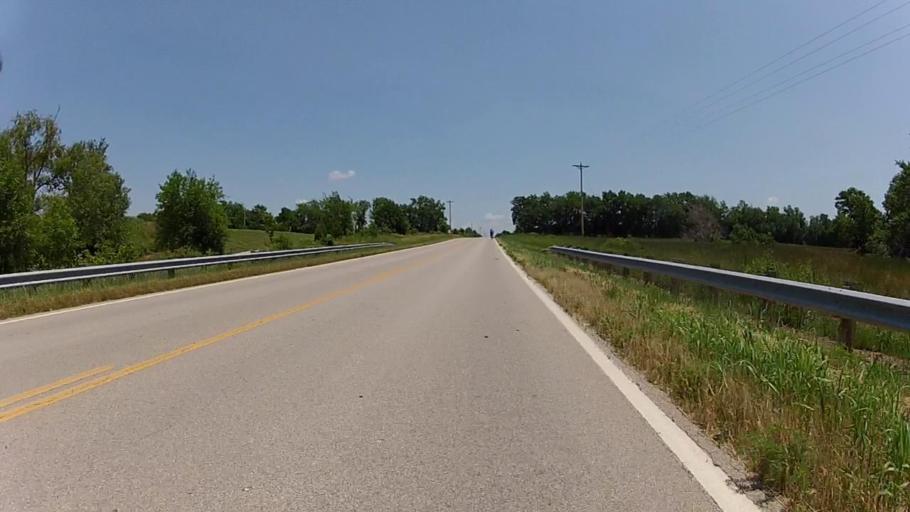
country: US
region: Kansas
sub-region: Montgomery County
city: Cherryvale
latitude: 37.1937
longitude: -95.5142
